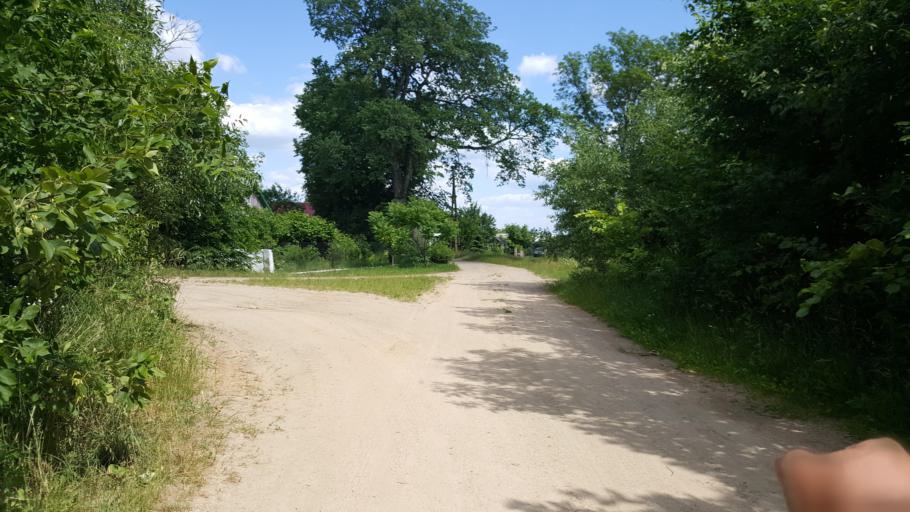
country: BY
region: Brest
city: Kamyanyuki
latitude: 52.5005
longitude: 23.7063
